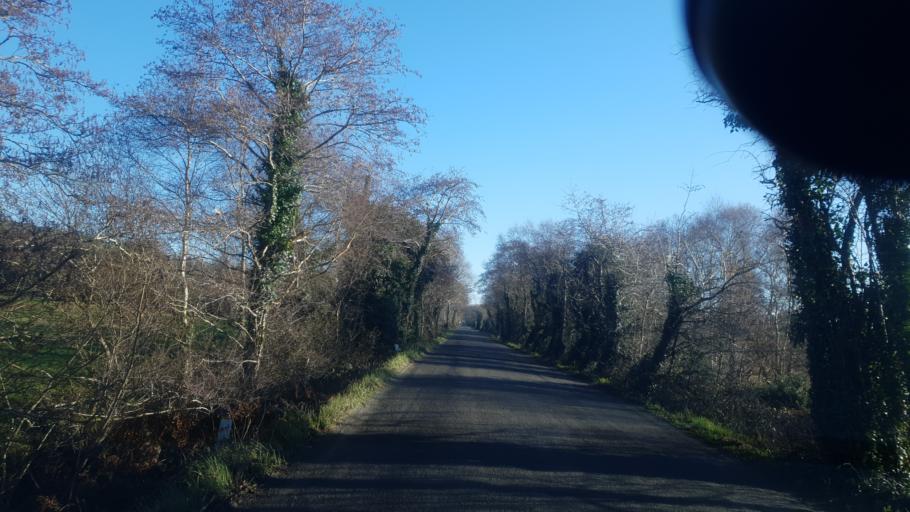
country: IE
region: Munster
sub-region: Ciarrai
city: Cill Airne
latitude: 52.1082
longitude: -9.4771
